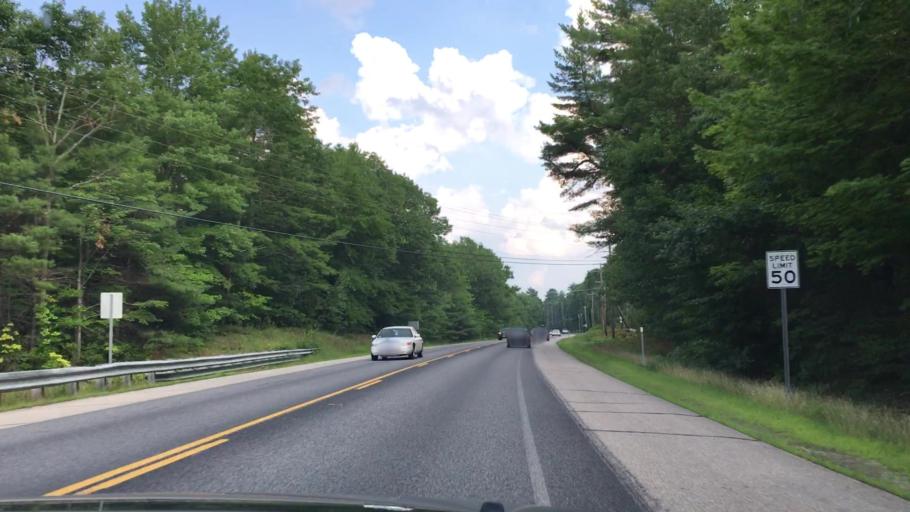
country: US
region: New Hampshire
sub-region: Strafford County
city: Farmington
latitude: 43.3831
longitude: -71.0718
